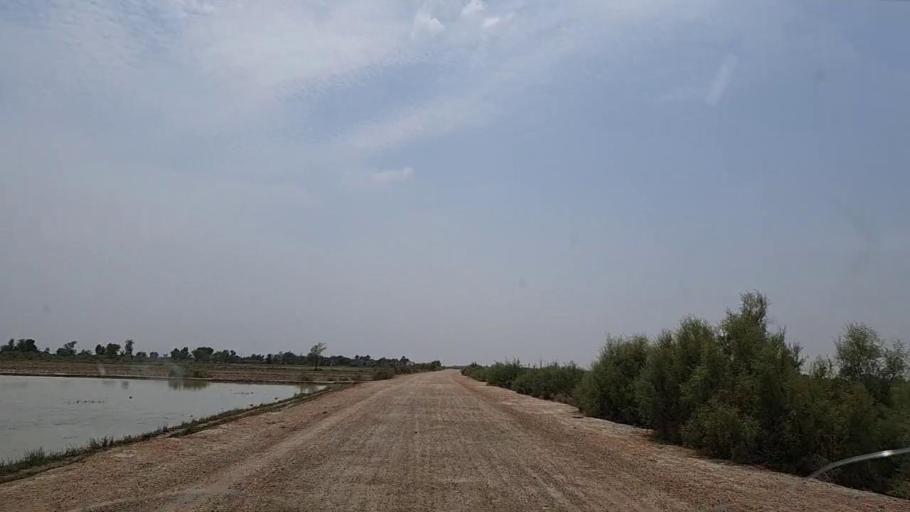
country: PK
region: Sindh
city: Phulji
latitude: 26.8814
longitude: 67.6745
